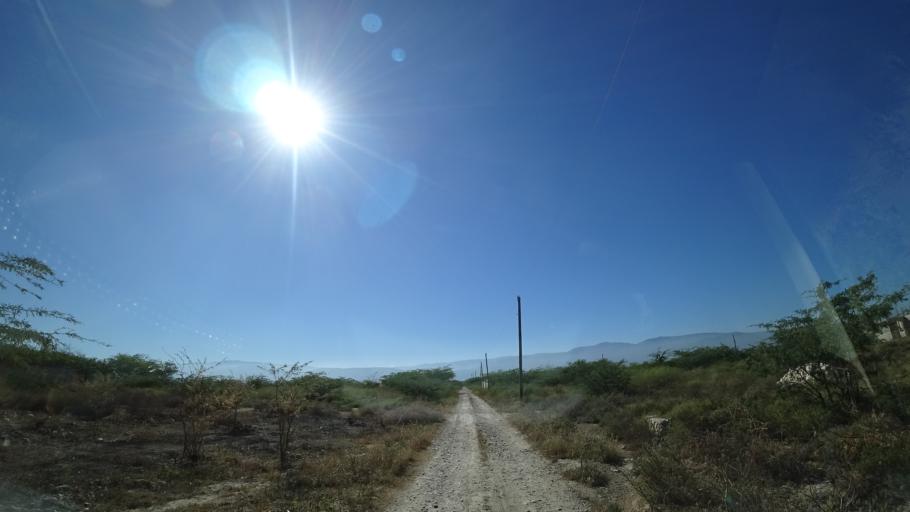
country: HT
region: Ouest
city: Croix des Bouquets
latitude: 18.6562
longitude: -72.2247
